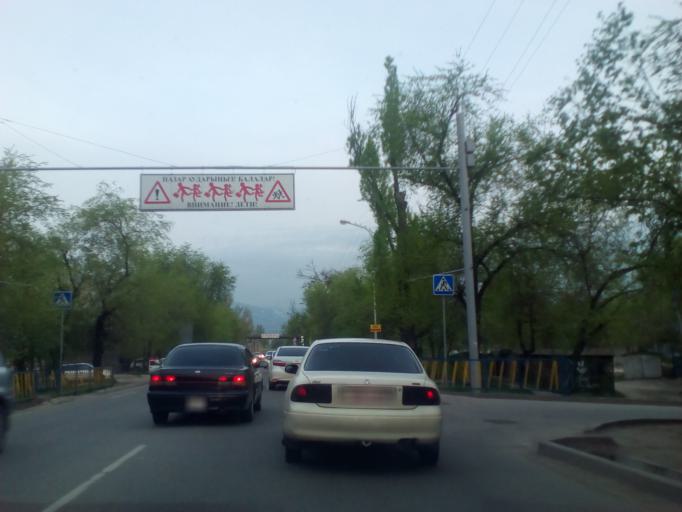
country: KZ
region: Almaty Qalasy
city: Almaty
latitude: 43.2351
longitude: 76.8248
